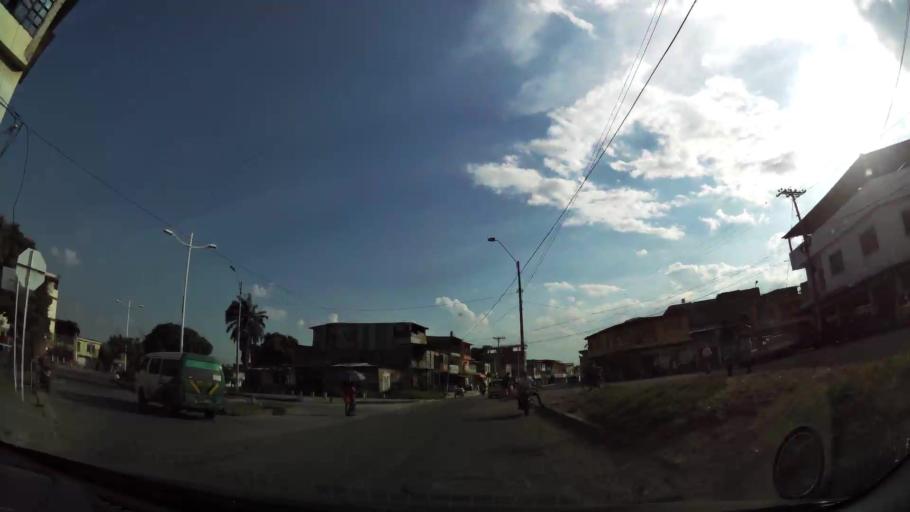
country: CO
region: Valle del Cauca
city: Cali
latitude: 3.4245
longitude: -76.4889
